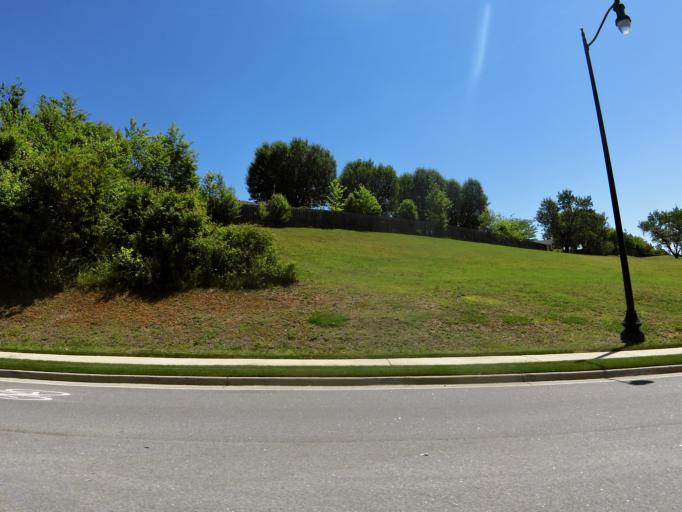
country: US
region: Georgia
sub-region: Columbia County
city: Martinez
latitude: 33.4971
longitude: -82.0313
